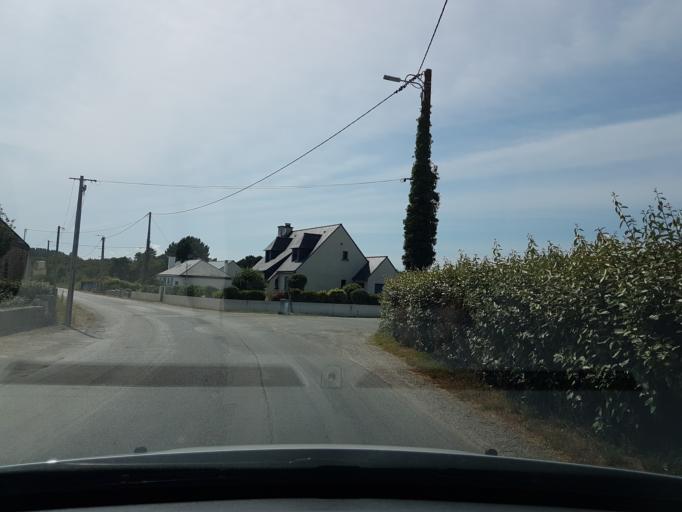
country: FR
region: Brittany
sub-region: Departement du Morbihan
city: Etel
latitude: 47.6779
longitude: -3.2145
